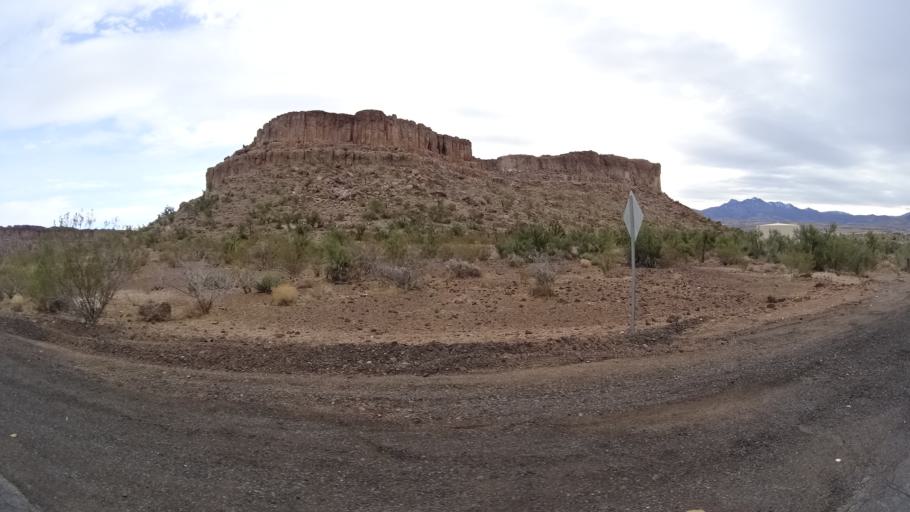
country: US
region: Arizona
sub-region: Mohave County
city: Kingman
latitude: 35.2060
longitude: -114.0812
